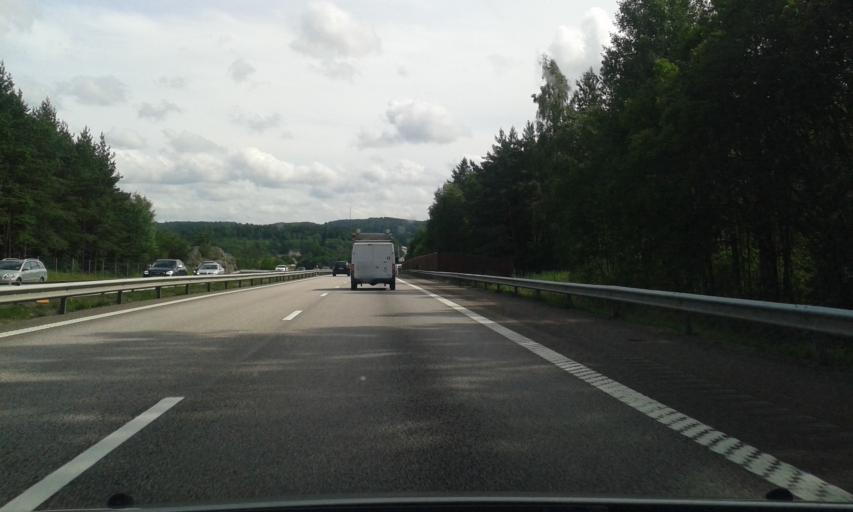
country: SE
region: Halland
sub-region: Kungsbacka Kommun
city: Fjaeras kyrkby
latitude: 57.4242
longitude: 12.1641
